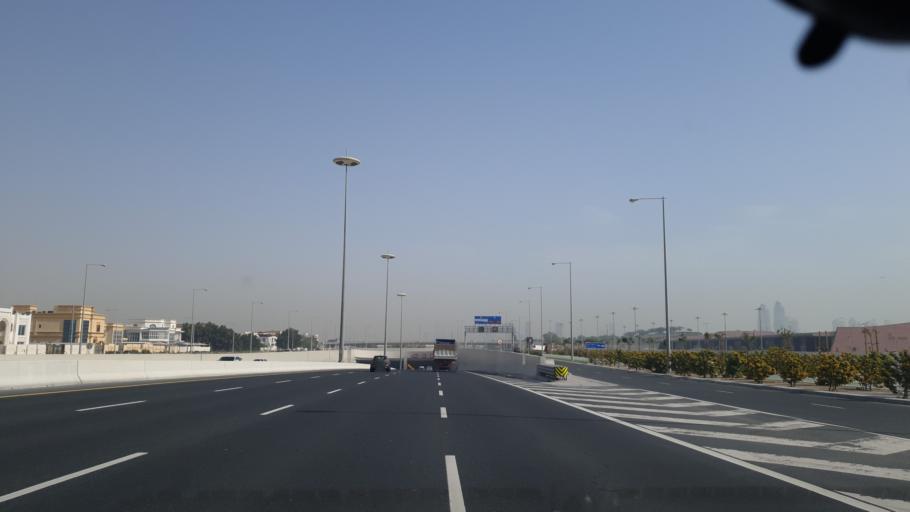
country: QA
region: Baladiyat ad Dawhah
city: Doha
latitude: 25.3466
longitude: 51.5205
